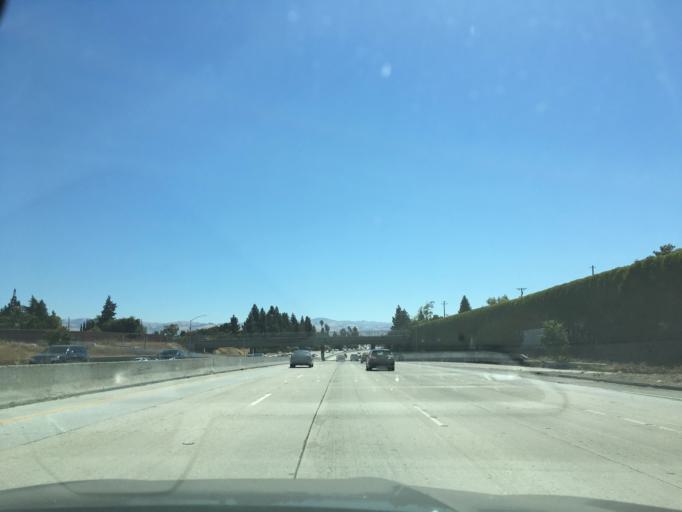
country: US
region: California
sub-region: Santa Clara County
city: Burbank
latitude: 37.3173
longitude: -121.9386
